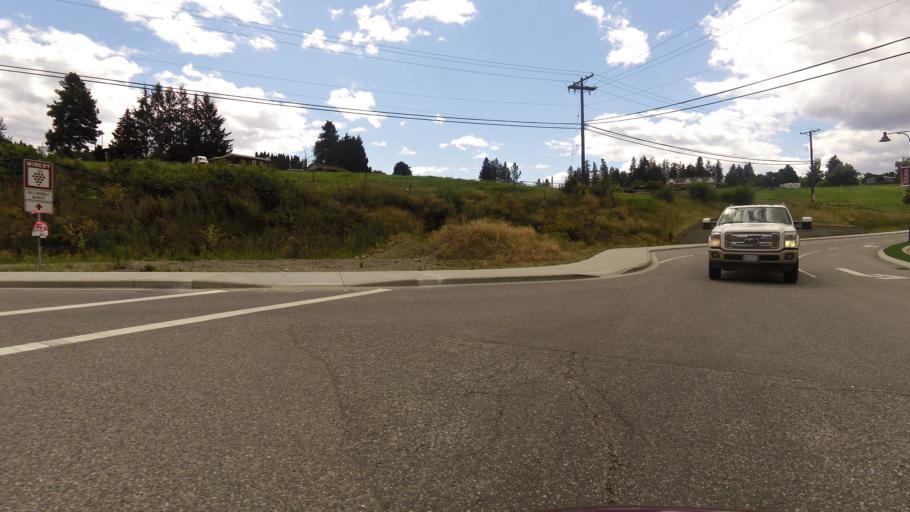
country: CA
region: British Columbia
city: West Kelowna
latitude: 49.8729
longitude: -119.5439
